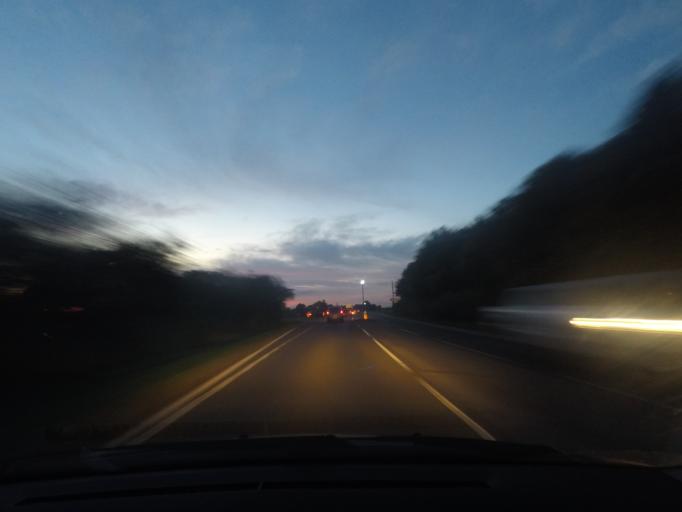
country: GB
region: England
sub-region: City of York
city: Elvington
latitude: 53.9501
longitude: -0.9412
